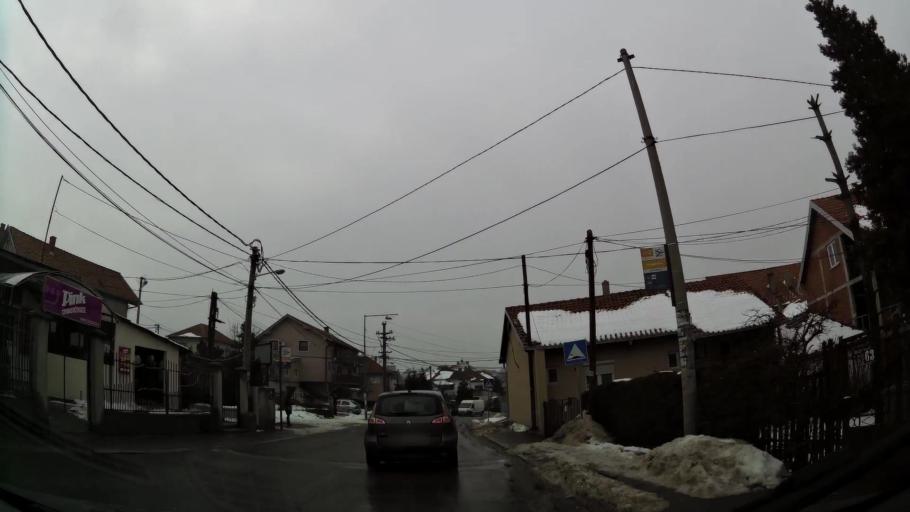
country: RS
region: Central Serbia
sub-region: Belgrade
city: Zvezdara
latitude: 44.7614
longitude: 20.5308
